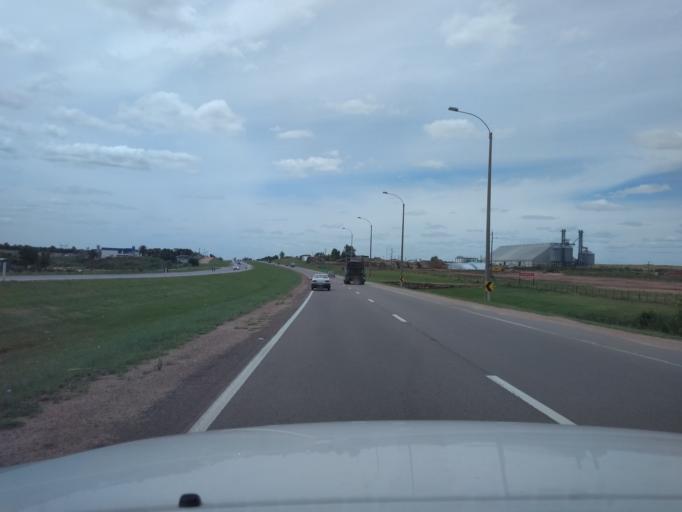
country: UY
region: Canelones
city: La Paz
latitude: -34.7480
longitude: -56.2538
